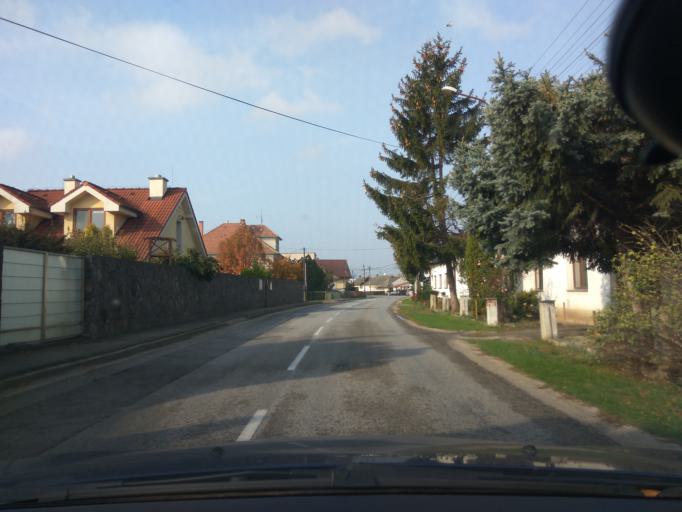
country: SK
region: Trnavsky
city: Vrbove
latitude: 48.6280
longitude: 17.7736
